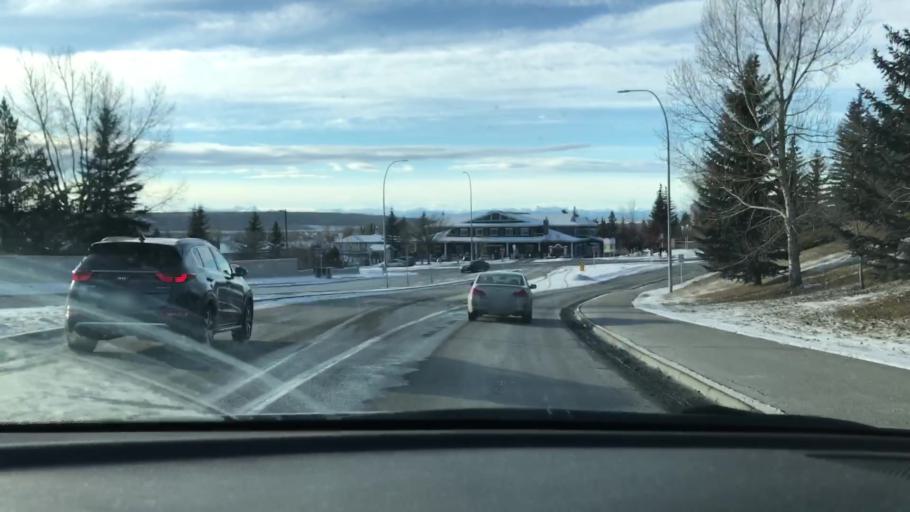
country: CA
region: Alberta
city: Calgary
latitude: 51.0163
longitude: -114.1743
